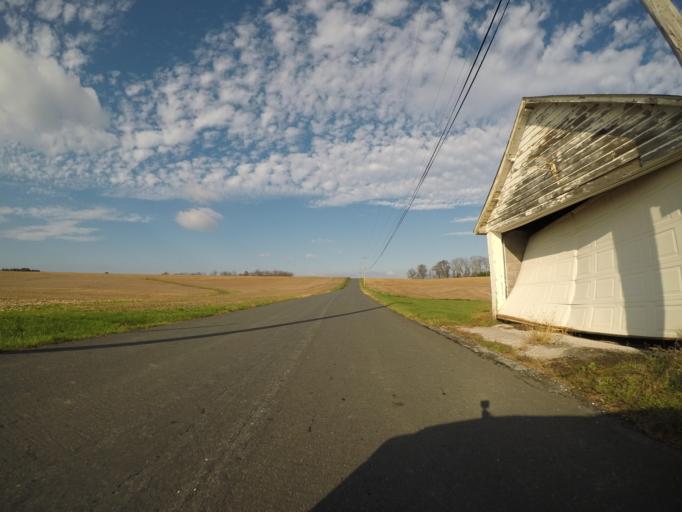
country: US
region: Maryland
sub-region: Carroll County
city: Hampstead
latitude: 39.5841
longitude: -76.8240
